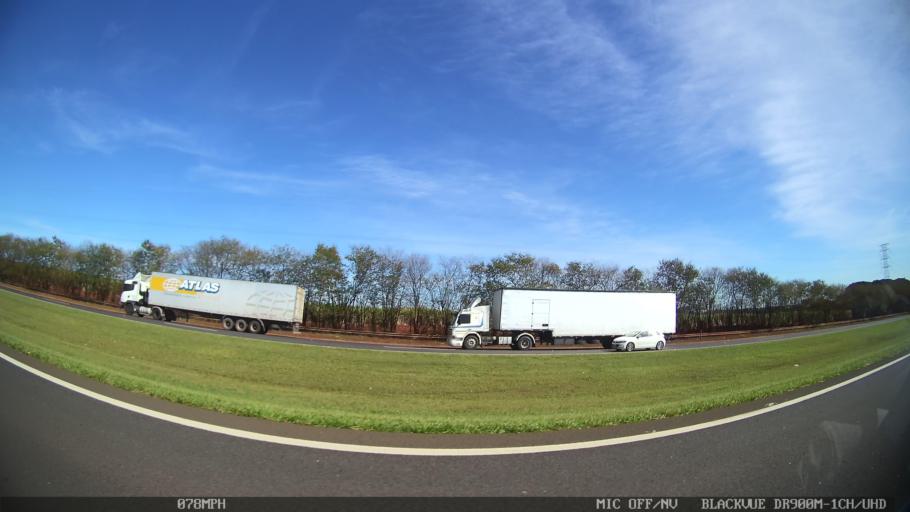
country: BR
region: Sao Paulo
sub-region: Araras
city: Araras
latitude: -22.3190
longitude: -47.3902
